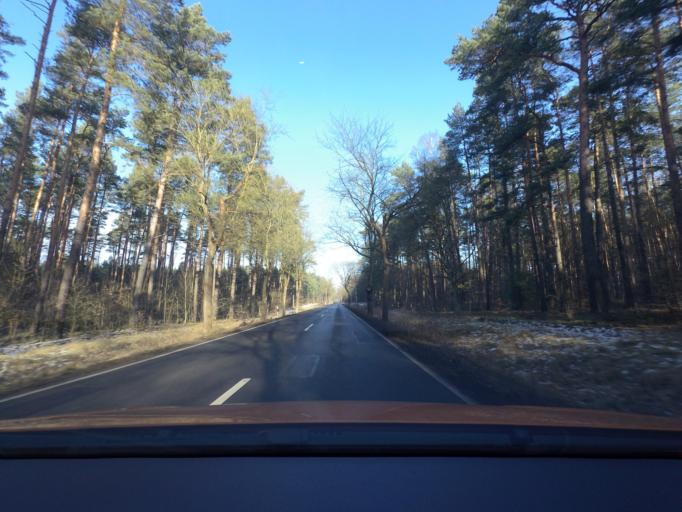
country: DE
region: Brandenburg
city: Glienicke
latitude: 52.6991
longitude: 13.3655
